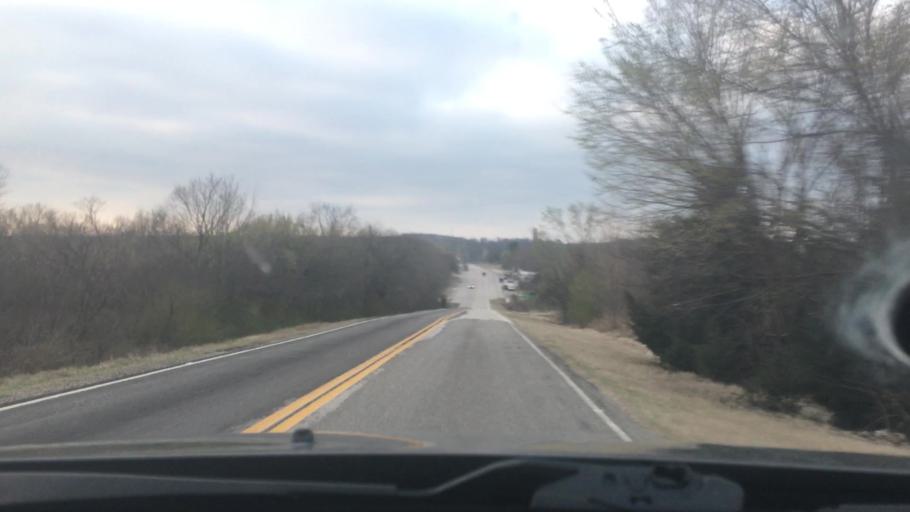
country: US
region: Oklahoma
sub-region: Pontotoc County
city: Ada
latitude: 34.6192
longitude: -96.6348
